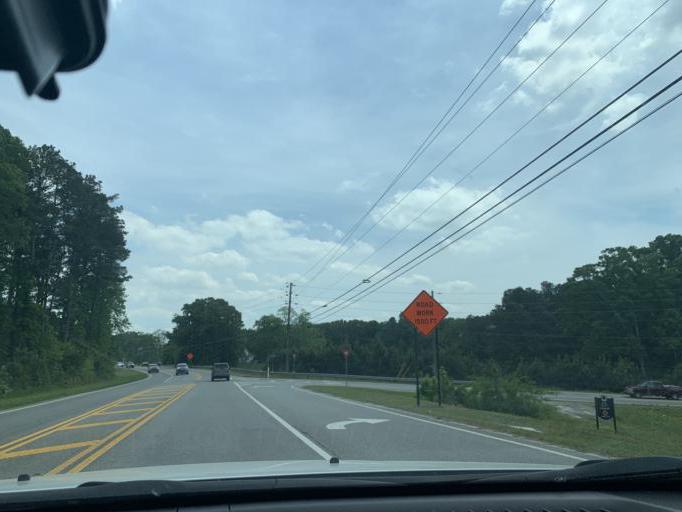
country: US
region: Georgia
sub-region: Forsyth County
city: Cumming
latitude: 34.1515
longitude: -84.1525
